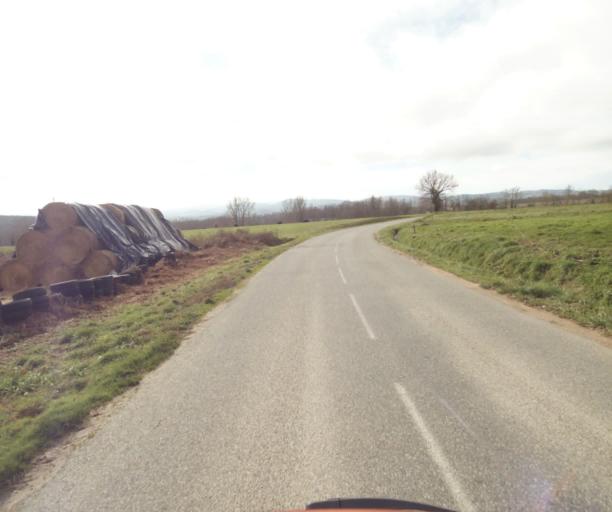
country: FR
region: Midi-Pyrenees
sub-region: Departement de l'Ariege
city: Pamiers
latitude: 43.1189
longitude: 1.5489
